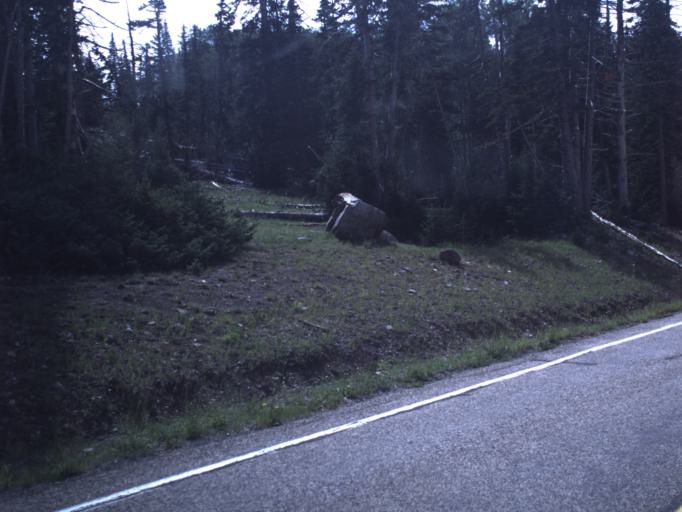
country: US
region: Utah
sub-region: Iron County
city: Cedar City
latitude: 37.5894
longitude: -112.8488
